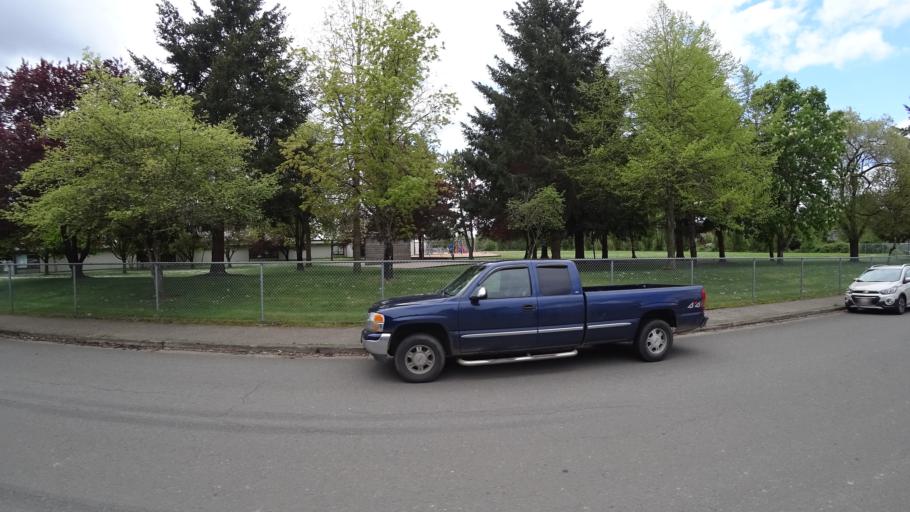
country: US
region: Oregon
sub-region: Washington County
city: Rockcreek
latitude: 45.5589
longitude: -122.8933
